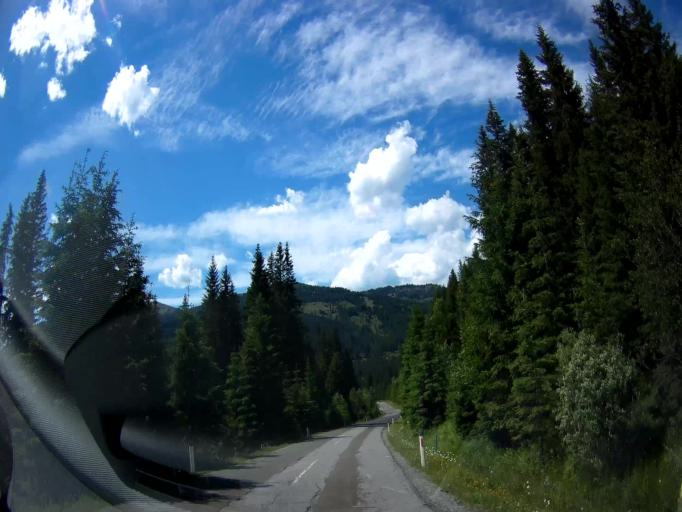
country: AT
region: Styria
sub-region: Politischer Bezirk Murau
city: Stadl an der Mur
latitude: 46.9728
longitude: 14.0117
